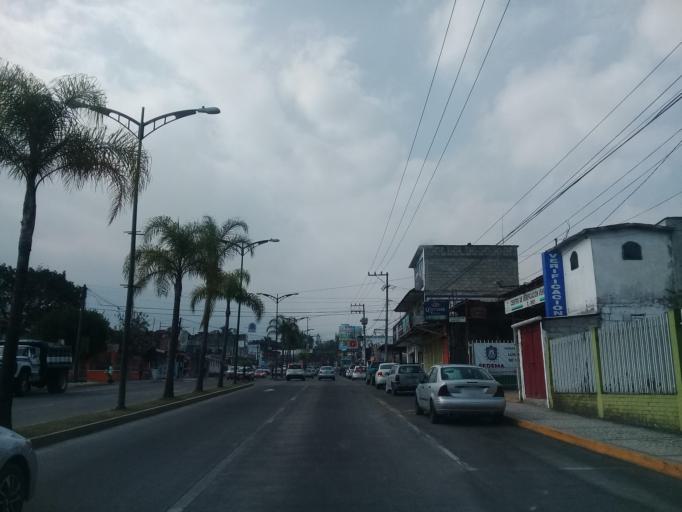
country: MX
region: Veracruz
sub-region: Ixhuatlancillo
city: Union y Progreso
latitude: 18.8678
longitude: -97.1129
